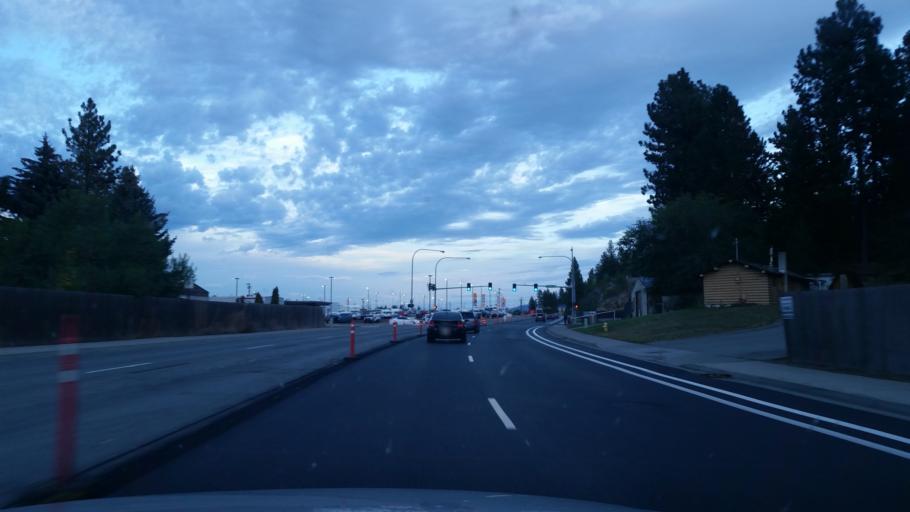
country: US
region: Washington
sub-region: Spokane County
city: Dishman
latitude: 47.6549
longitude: -117.2962
